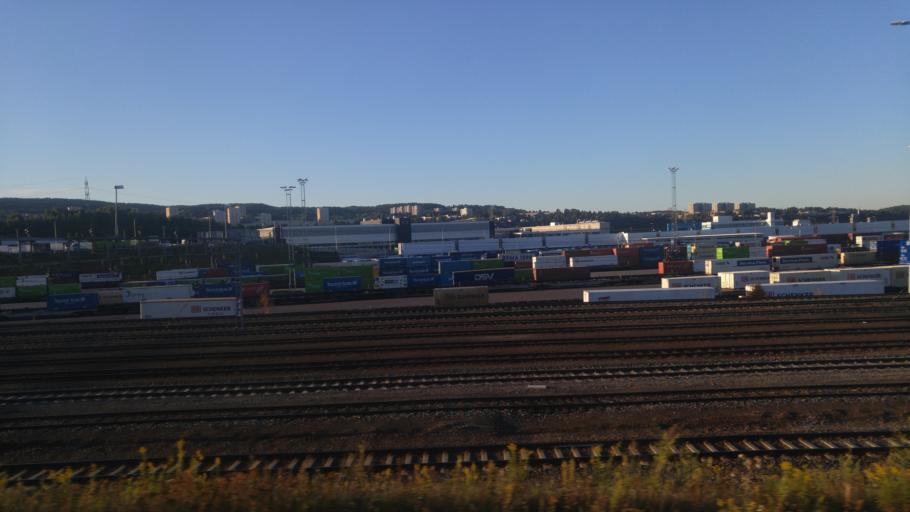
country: NO
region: Akershus
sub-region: Lorenskog
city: Kjenn
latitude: 59.9391
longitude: 10.8496
